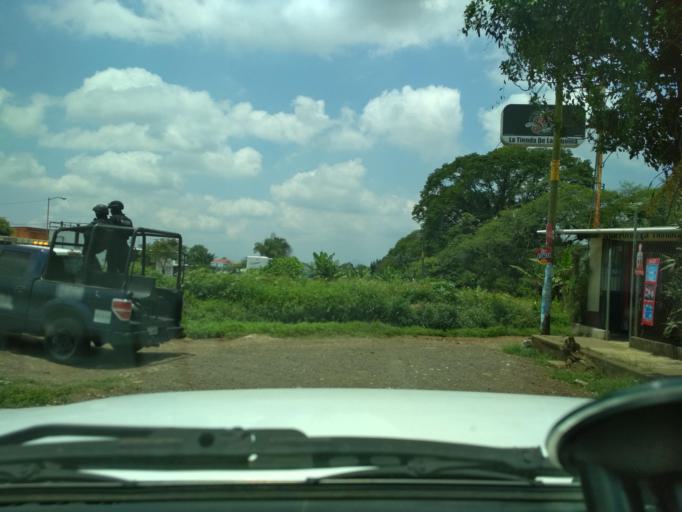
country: MX
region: Veracruz
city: Tocuila
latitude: 18.9515
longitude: -97.0181
